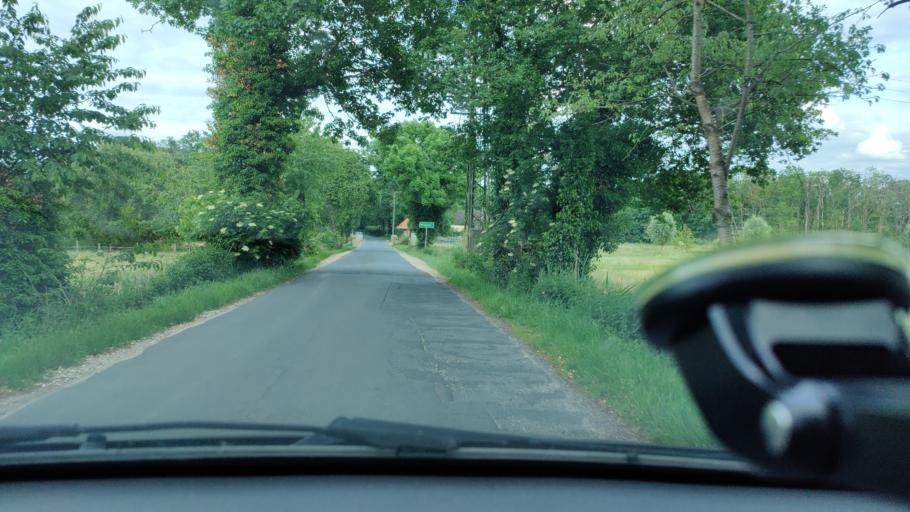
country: DE
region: North Rhine-Westphalia
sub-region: Regierungsbezirk Dusseldorf
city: Goch
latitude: 51.6781
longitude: 6.1935
